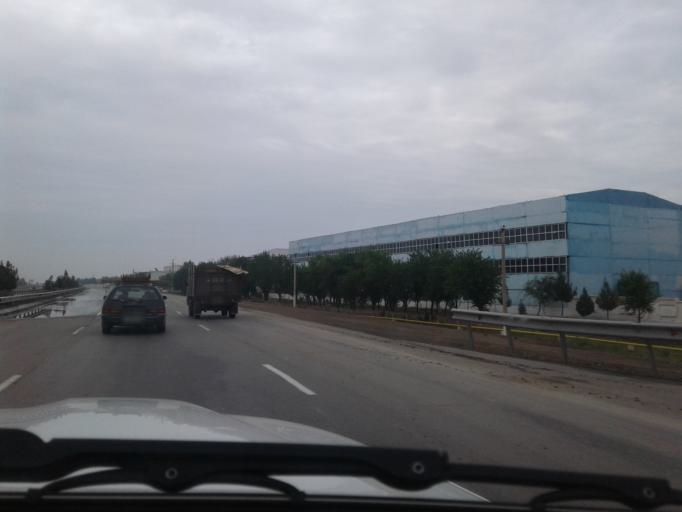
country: TM
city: Murgab
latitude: 37.6110
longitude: 61.9597
